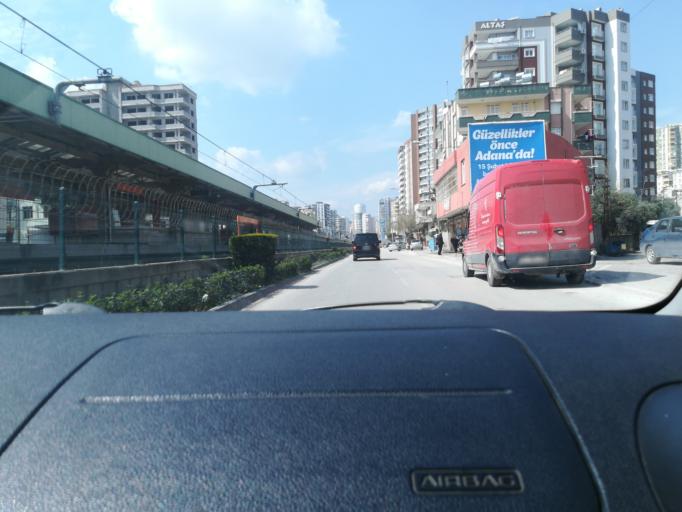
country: TR
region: Adana
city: Seyhan
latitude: 37.0269
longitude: 35.2970
